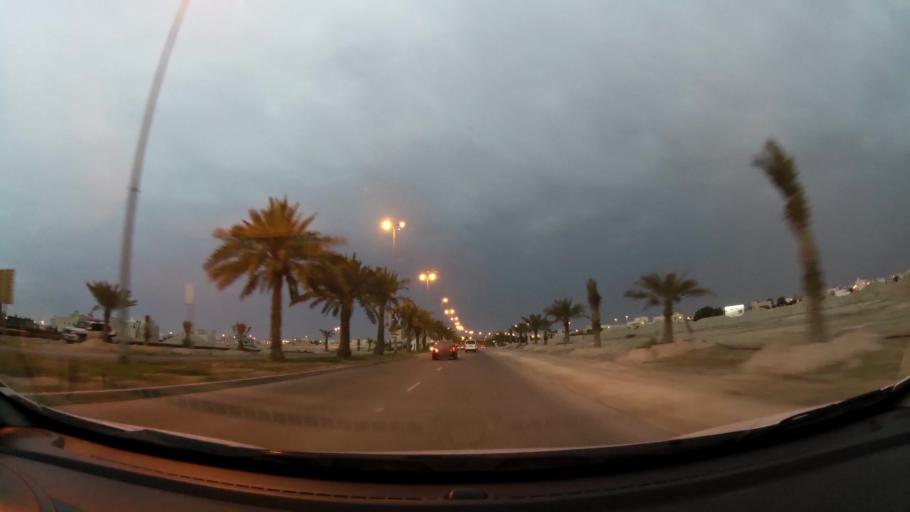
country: BH
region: Central Governorate
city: Madinat Hamad
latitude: 26.1418
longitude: 50.5026
